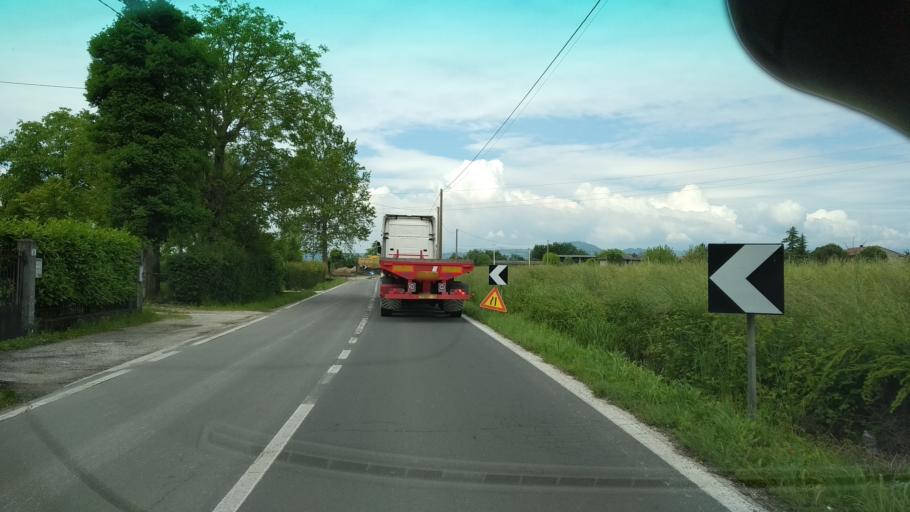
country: IT
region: Veneto
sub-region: Provincia di Vicenza
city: Monticello Conte Otto
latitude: 45.5986
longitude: 11.5459
